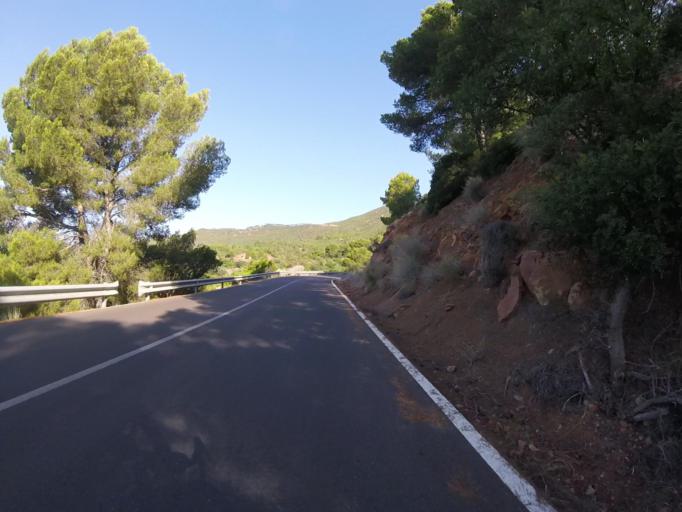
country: ES
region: Valencia
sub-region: Provincia de Castello
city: Benicassim
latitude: 40.0784
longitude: 0.0430
